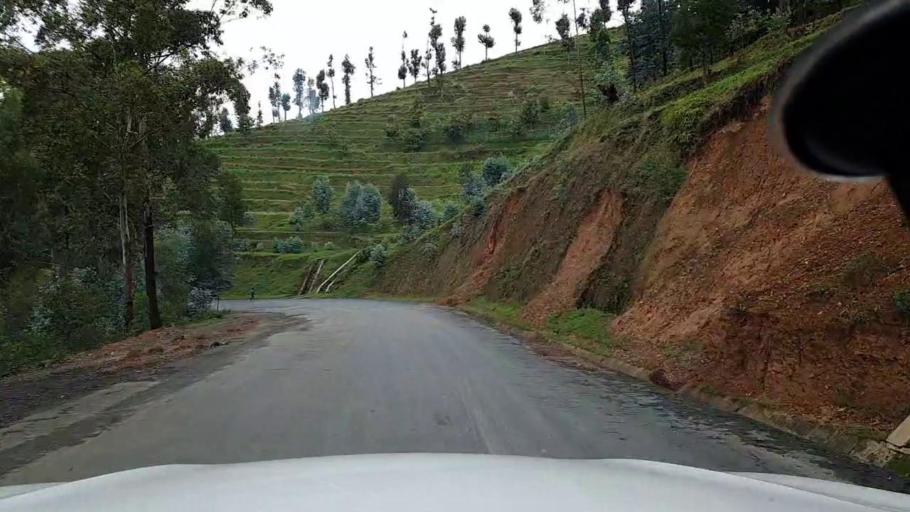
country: RW
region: Western Province
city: Kibuye
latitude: -2.0668
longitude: 29.5396
